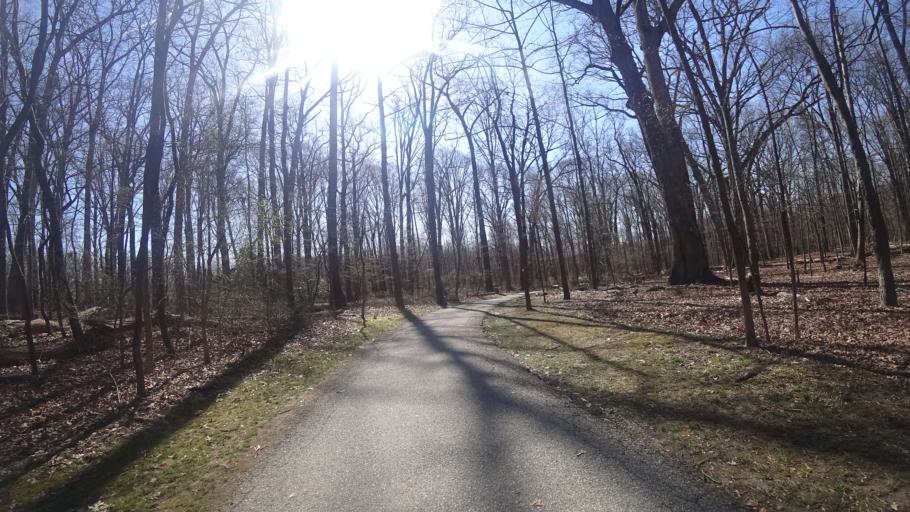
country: US
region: Maryland
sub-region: Montgomery County
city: Kemp Mill
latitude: 39.0439
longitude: -77.0361
